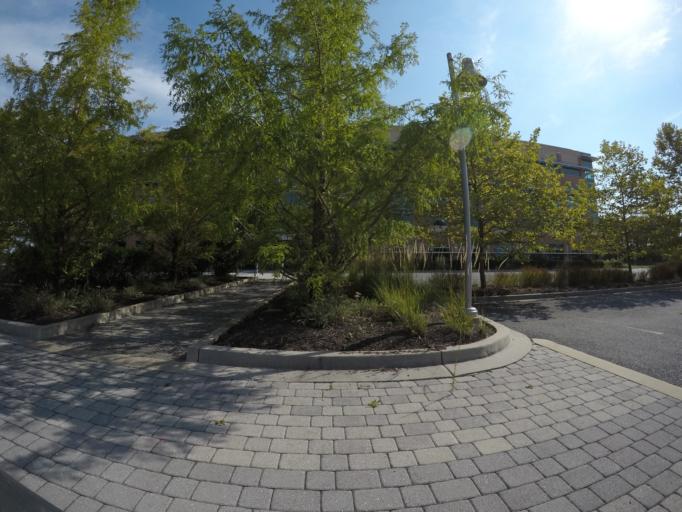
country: US
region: Maryland
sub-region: Harford County
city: Aberdeen
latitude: 39.5049
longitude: -76.1479
